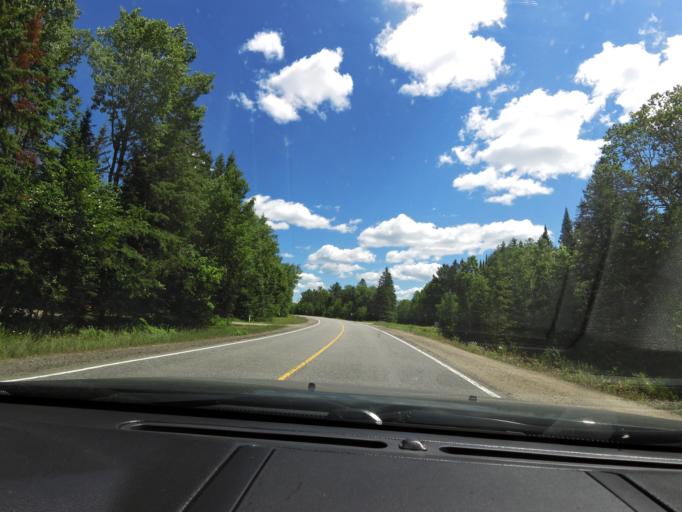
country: CA
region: Ontario
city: Huntsville
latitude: 45.5427
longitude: -79.2645
